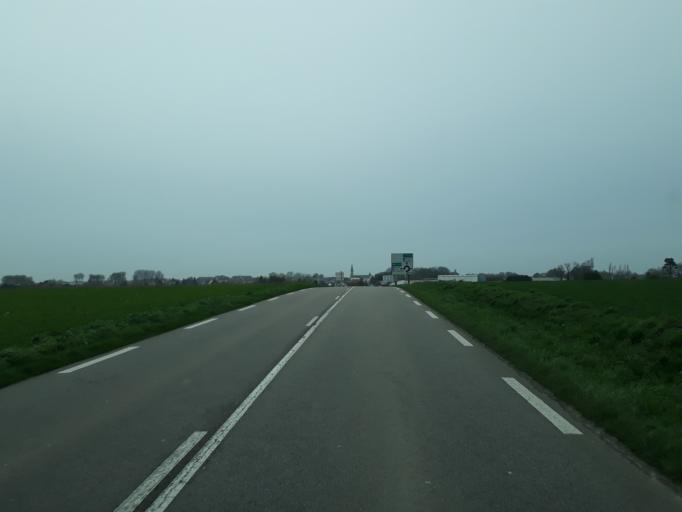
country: FR
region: Haute-Normandie
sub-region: Departement de la Seine-Maritime
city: Goderville
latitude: 49.6381
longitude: 0.3813
